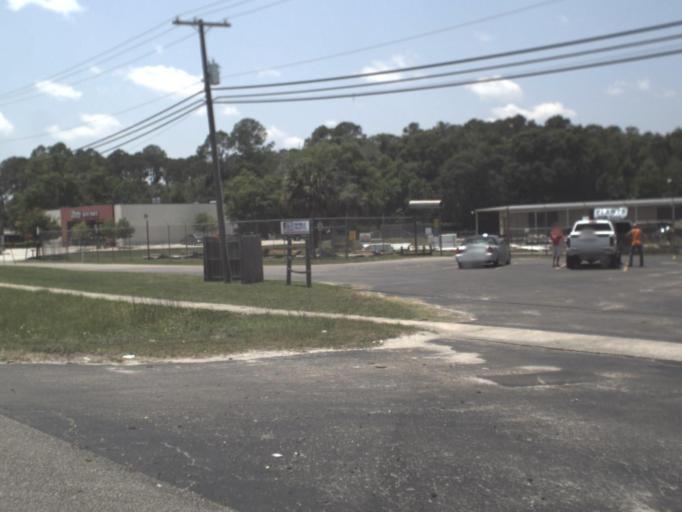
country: US
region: Florida
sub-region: Bradford County
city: Starke
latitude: 29.9359
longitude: -82.1131
